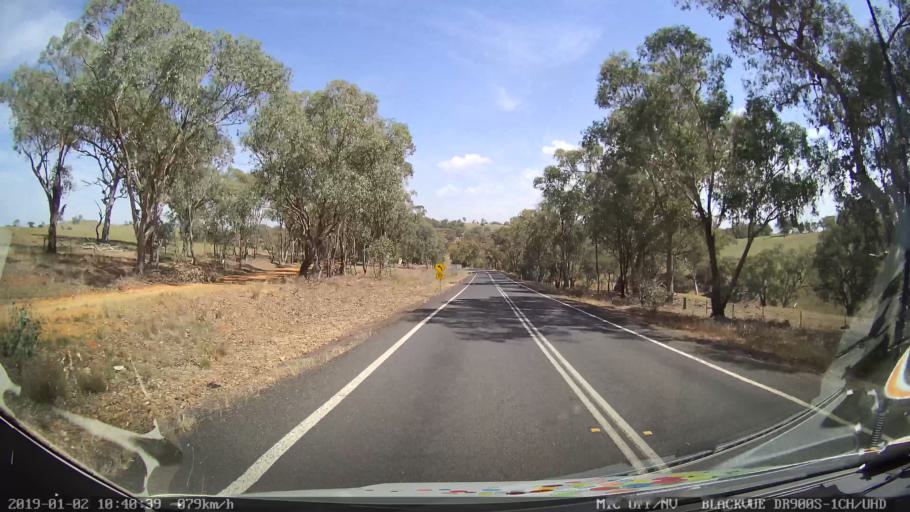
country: AU
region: New South Wales
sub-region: Cootamundra
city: Cootamundra
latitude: -34.8000
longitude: 148.3143
